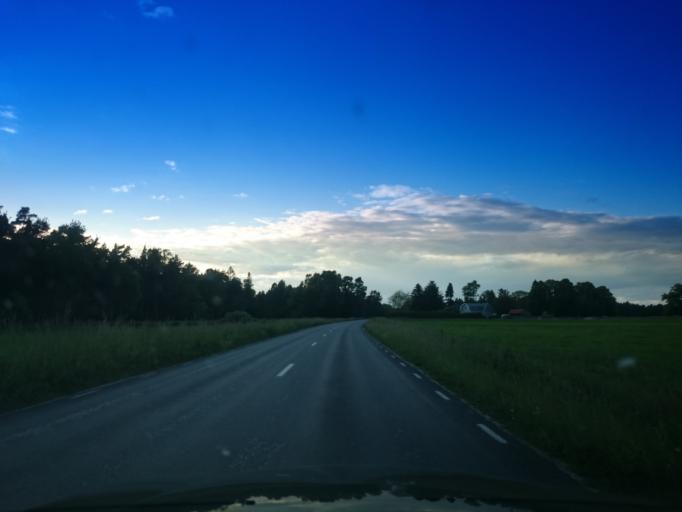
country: SE
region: Gotland
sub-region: Gotland
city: Hemse
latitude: 57.3264
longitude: 18.3816
